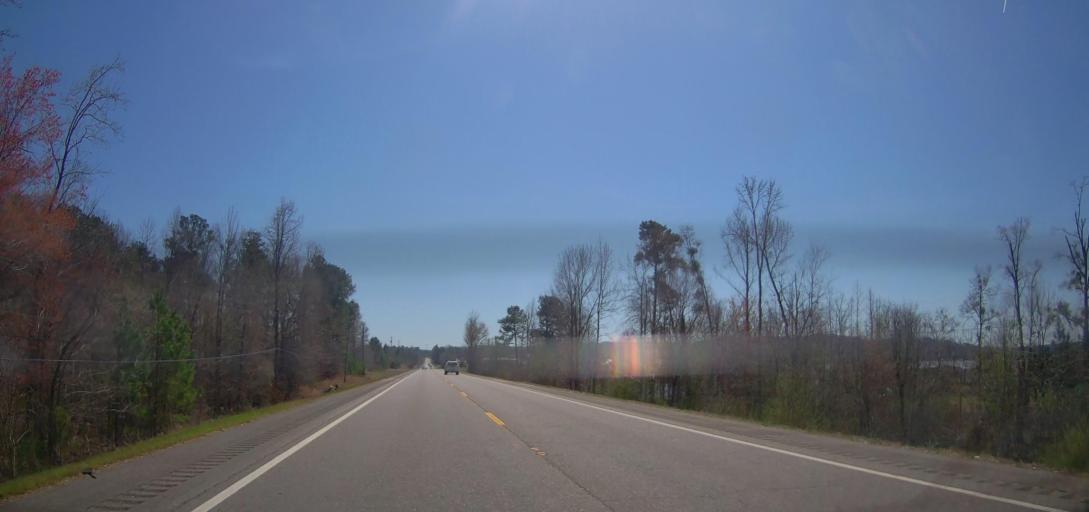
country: US
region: Alabama
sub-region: Calhoun County
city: Ohatchee
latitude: 33.8358
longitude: -86.0490
